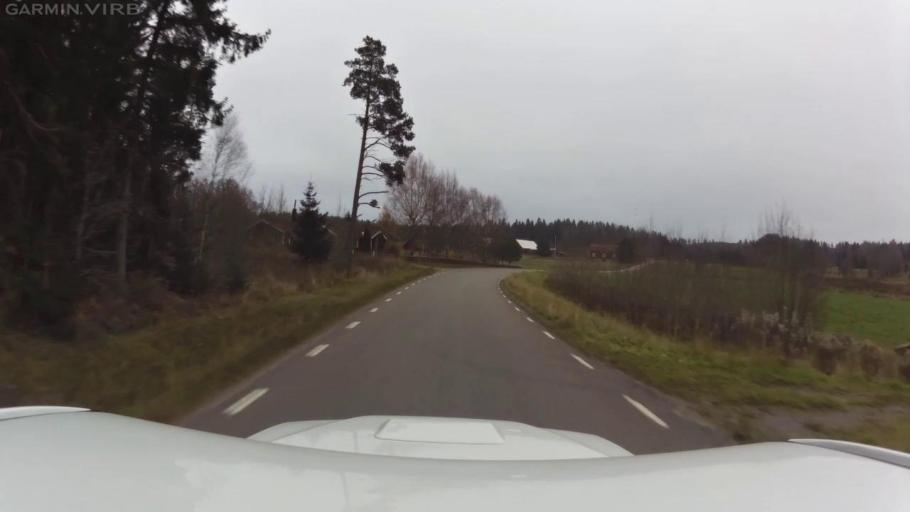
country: SE
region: OEstergoetland
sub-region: Linkopings Kommun
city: Vikingstad
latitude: 58.2201
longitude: 15.3988
